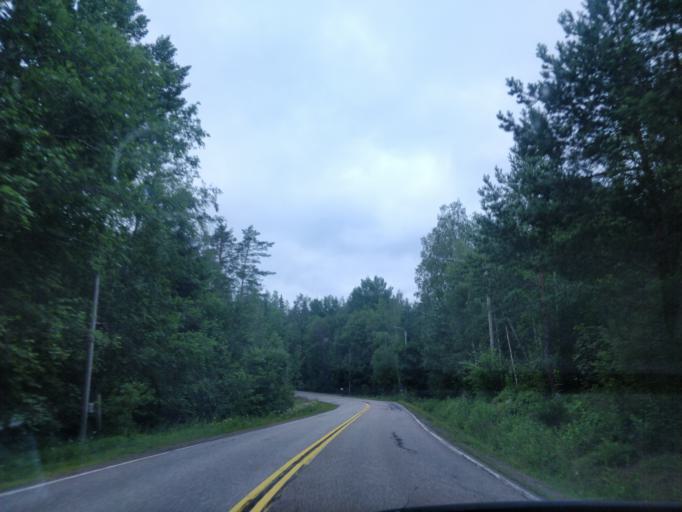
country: FI
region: Uusimaa
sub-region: Helsinki
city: Kauniainen
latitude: 60.3028
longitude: 24.6993
